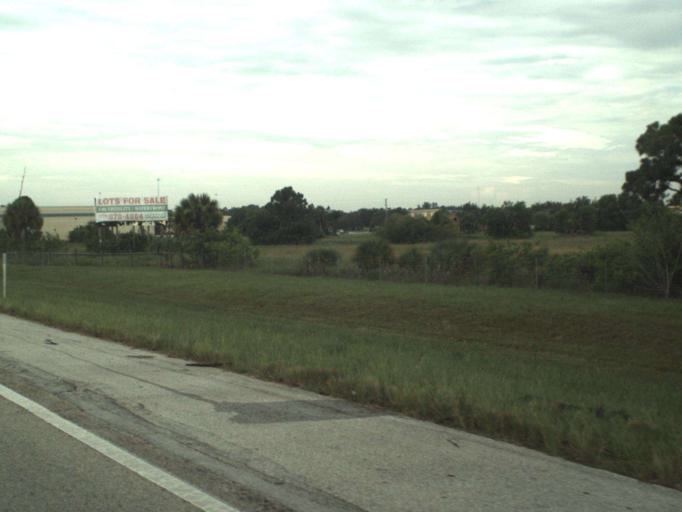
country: US
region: Florida
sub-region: Martin County
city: Palm City
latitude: 27.1142
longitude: -80.2644
